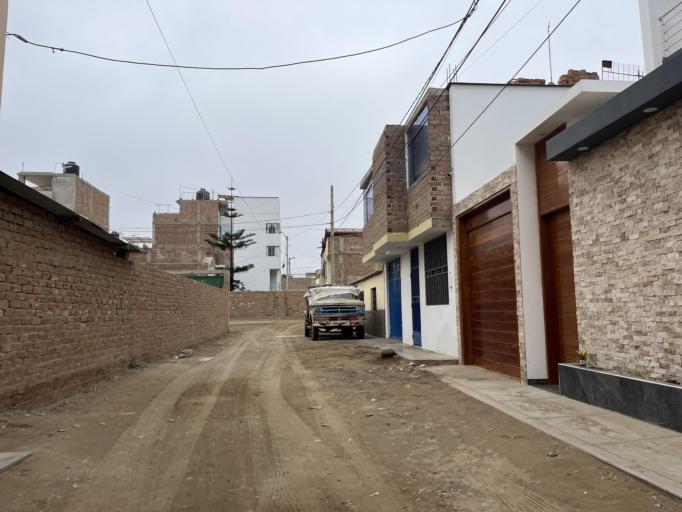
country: PE
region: La Libertad
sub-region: Provincia de Trujillo
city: La Esperanza
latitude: -8.0879
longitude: -79.0513
